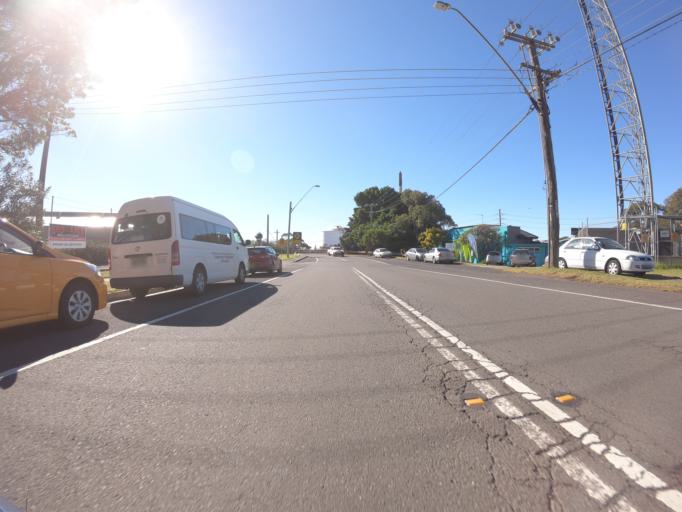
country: AU
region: New South Wales
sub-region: Wollongong
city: Port Kembla
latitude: -34.4785
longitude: 150.9032
